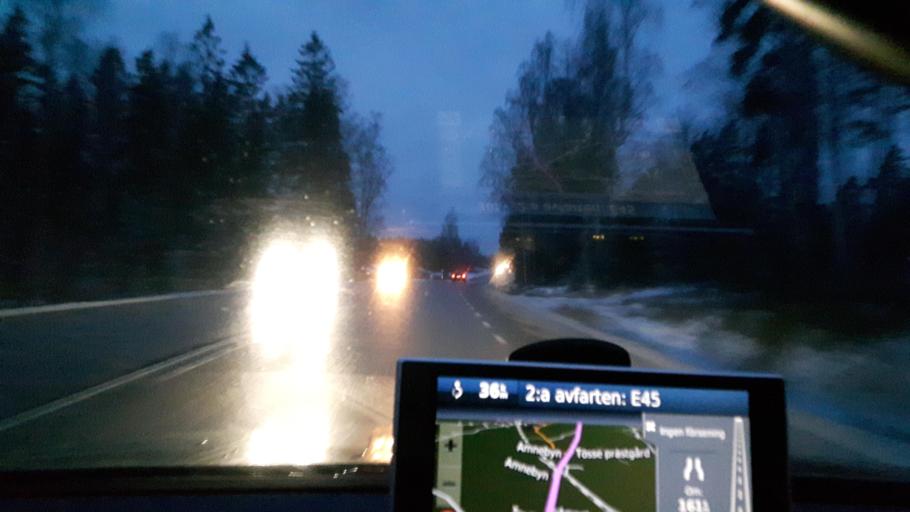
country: SE
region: Vaestra Goetaland
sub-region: Amals Kommun
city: Amal
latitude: 58.9861
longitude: 12.6631
